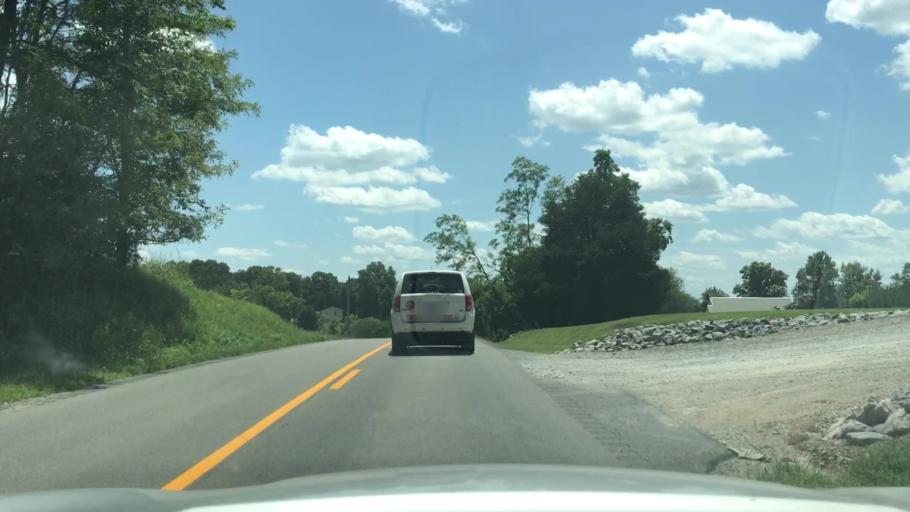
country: US
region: Kentucky
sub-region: Christian County
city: Hopkinsville
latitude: 36.9052
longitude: -87.4464
